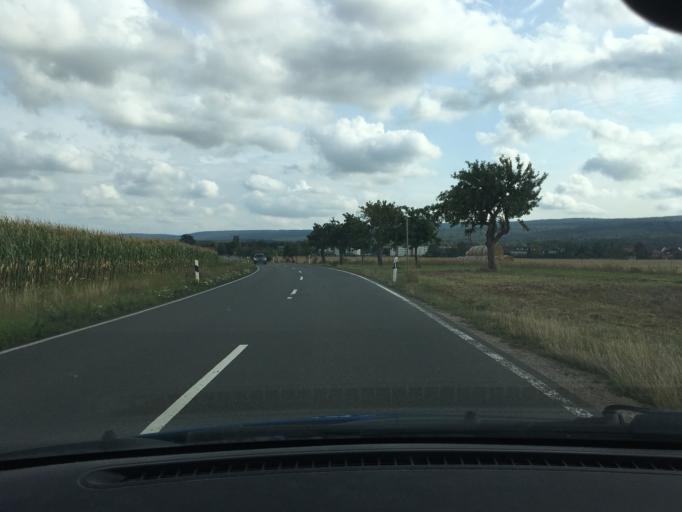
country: DE
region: Lower Saxony
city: Egestorf
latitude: 52.2961
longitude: 9.5049
